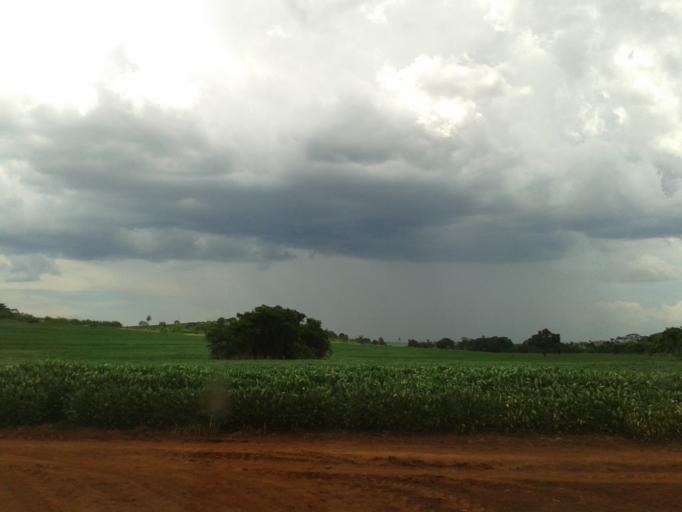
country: BR
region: Minas Gerais
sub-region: Centralina
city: Centralina
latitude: -18.6801
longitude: -49.2171
